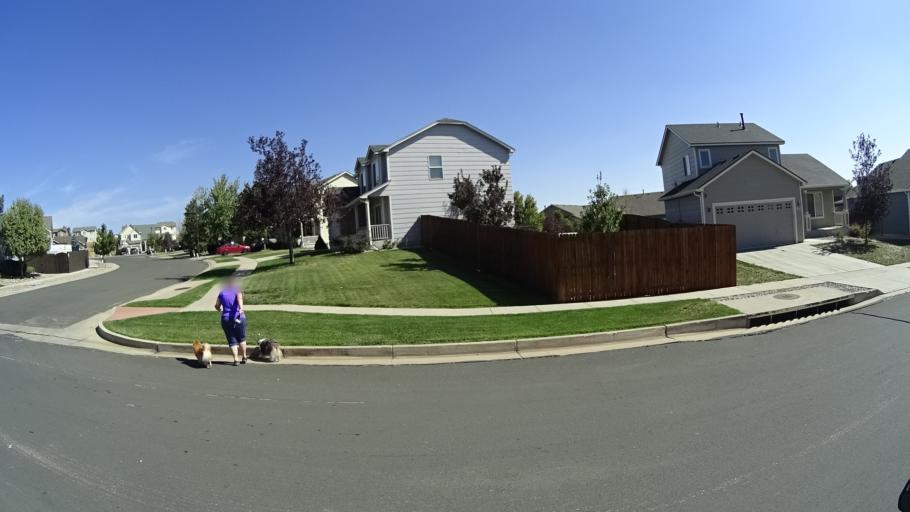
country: US
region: Colorado
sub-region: El Paso County
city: Cimarron Hills
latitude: 38.8963
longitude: -104.6911
